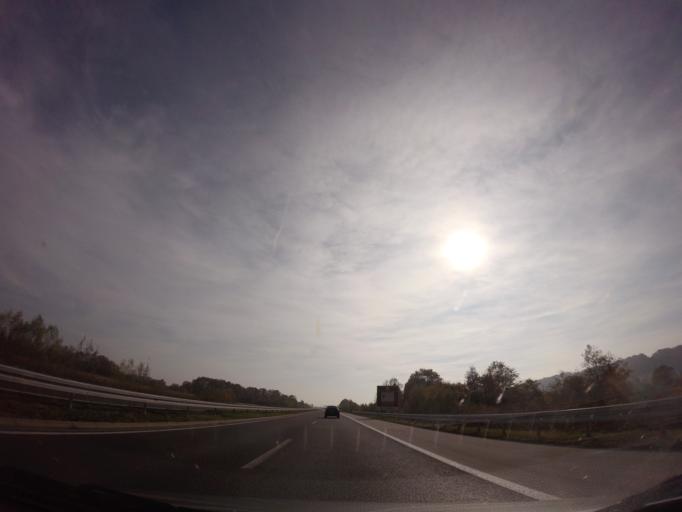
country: HR
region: Zagrebacka
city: Brckovljani
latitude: 45.9347
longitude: 16.2695
